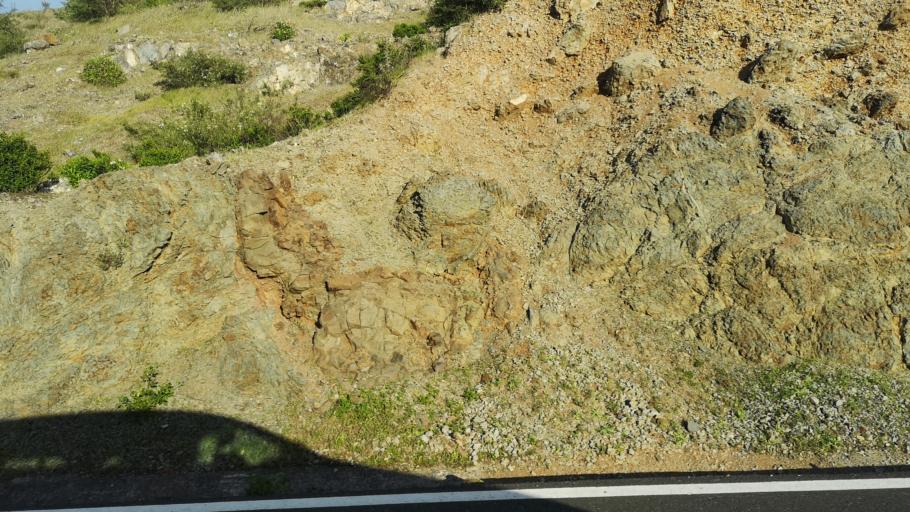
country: ES
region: Canary Islands
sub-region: Provincia de Santa Cruz de Tenerife
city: Alajero
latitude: 28.0920
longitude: -17.2486
